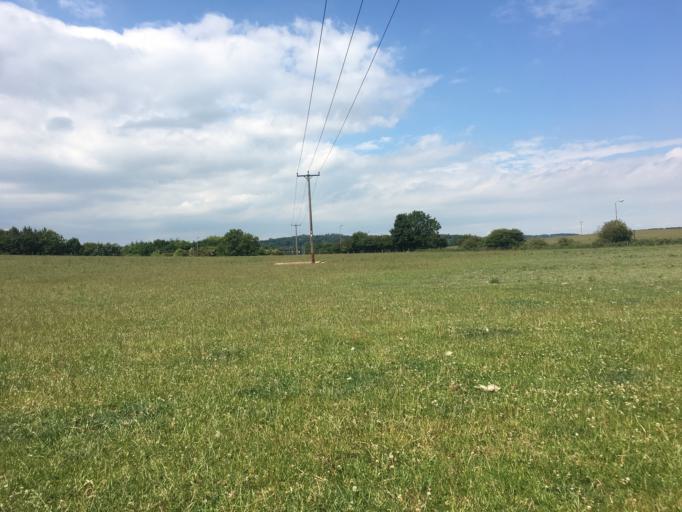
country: GB
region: England
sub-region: Northumberland
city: Belford
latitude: 55.5985
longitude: -1.8002
